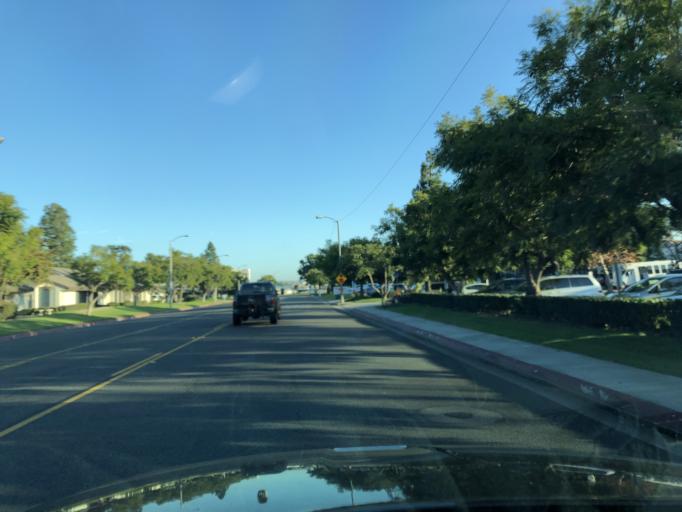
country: US
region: California
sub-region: Orange County
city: Irvine
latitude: 33.6773
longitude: -117.8753
